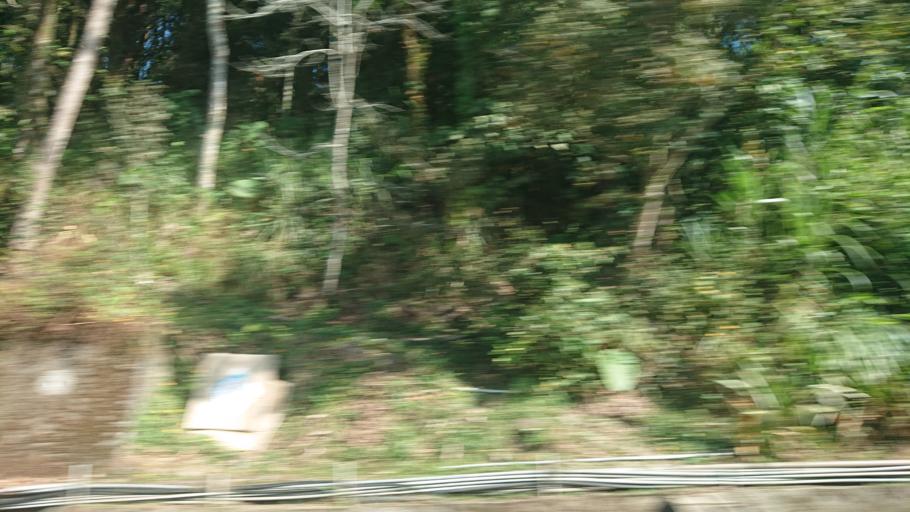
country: TW
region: Taiwan
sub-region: Chiayi
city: Jiayi Shi
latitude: 23.4716
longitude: 120.7049
